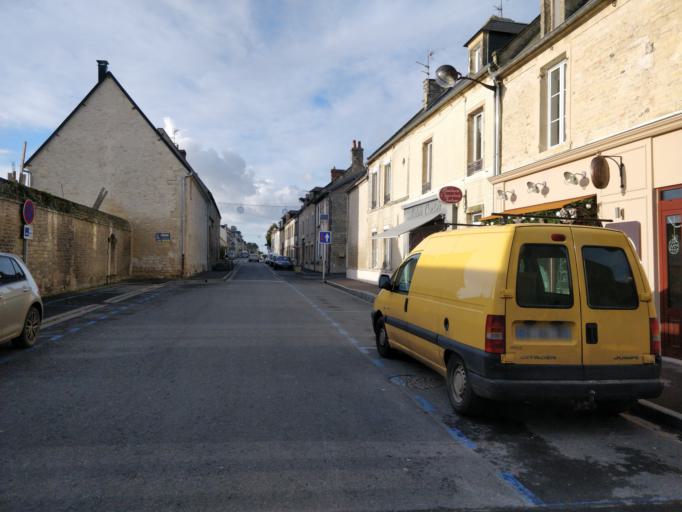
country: FR
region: Lower Normandy
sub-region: Departement du Calvados
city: Saint-Manvieu
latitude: 49.2119
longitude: -0.5172
